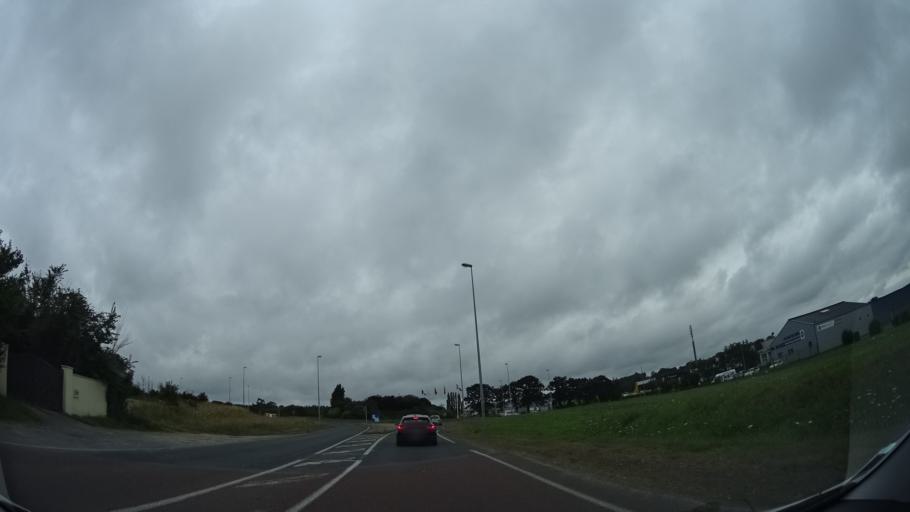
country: FR
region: Lower Normandy
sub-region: Departement de la Manche
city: La Haye-du-Puits
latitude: 49.2777
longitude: -1.5407
